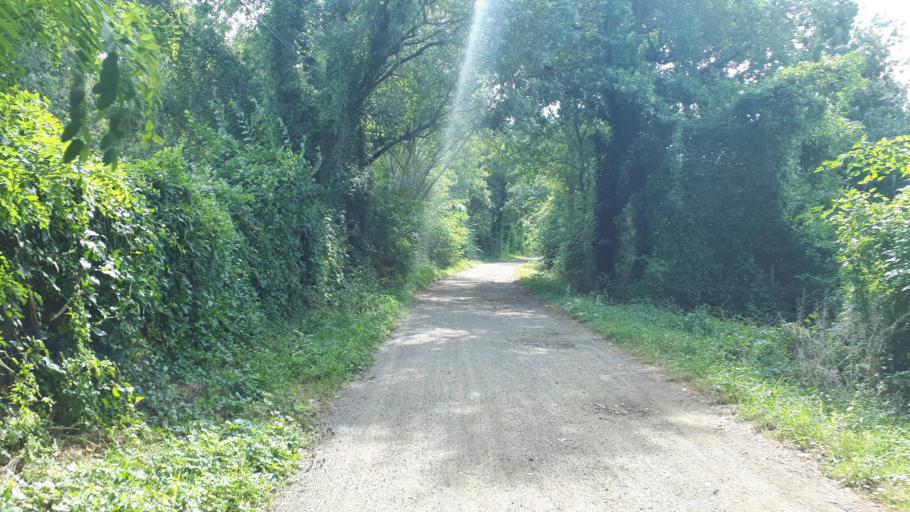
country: FR
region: Pays de la Loire
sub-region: Departement de Maine-et-Loire
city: Saint-Lambert-du-Lattay
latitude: 47.3242
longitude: -0.6577
